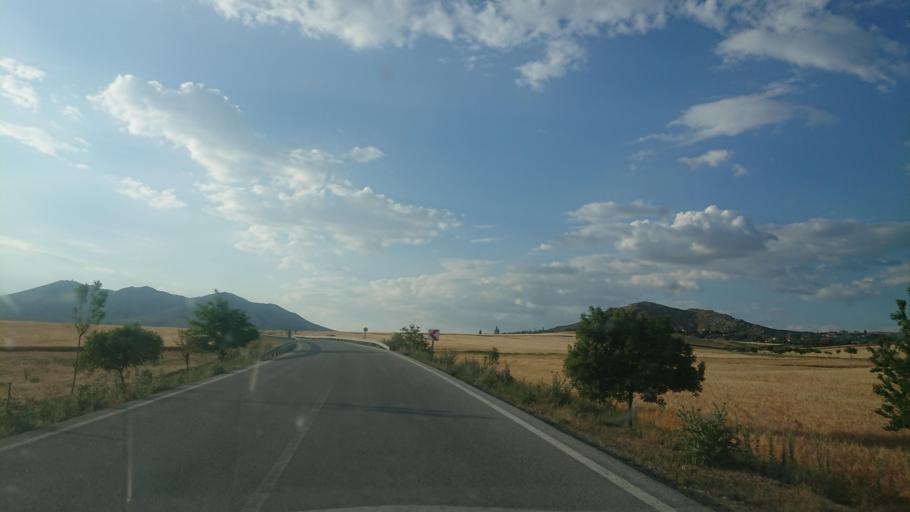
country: TR
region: Aksaray
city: Balci
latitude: 38.5800
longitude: 34.1052
